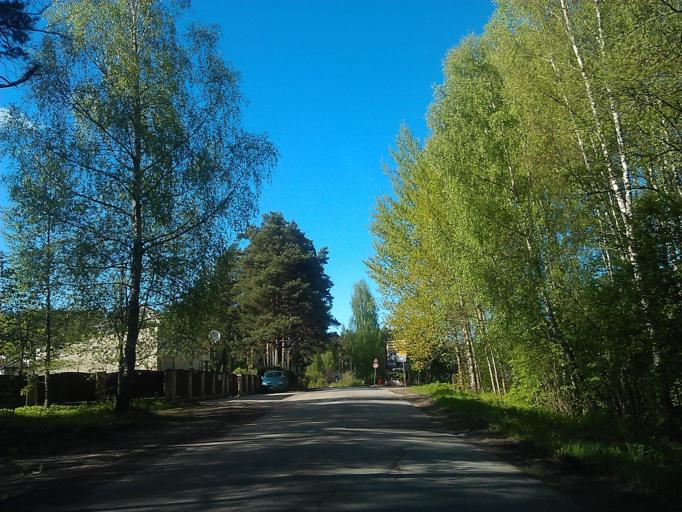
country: LV
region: Riga
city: Bergi
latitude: 57.0129
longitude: 24.2596
